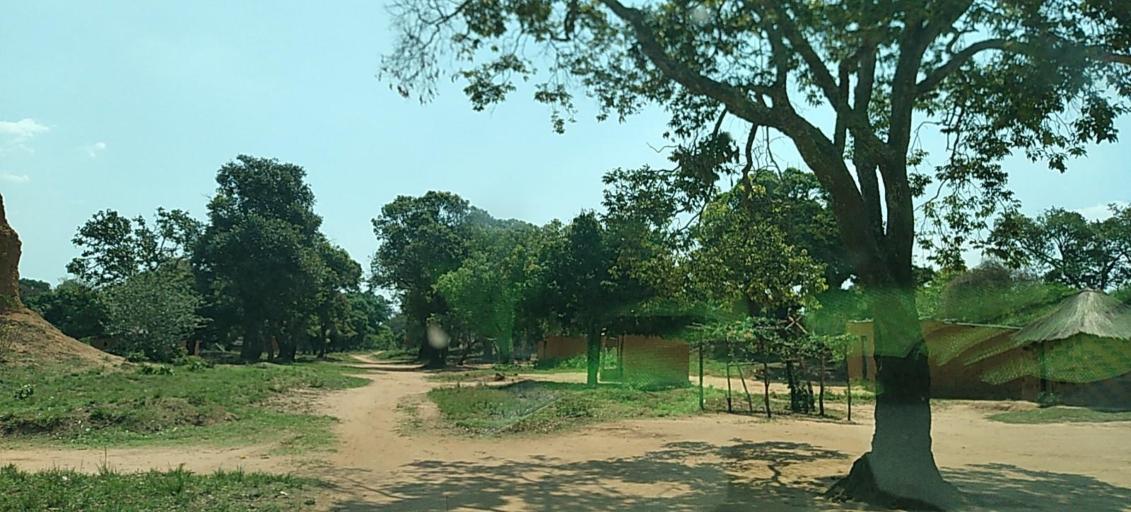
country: CD
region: Katanga
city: Kolwezi
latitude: -11.2790
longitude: 25.1302
